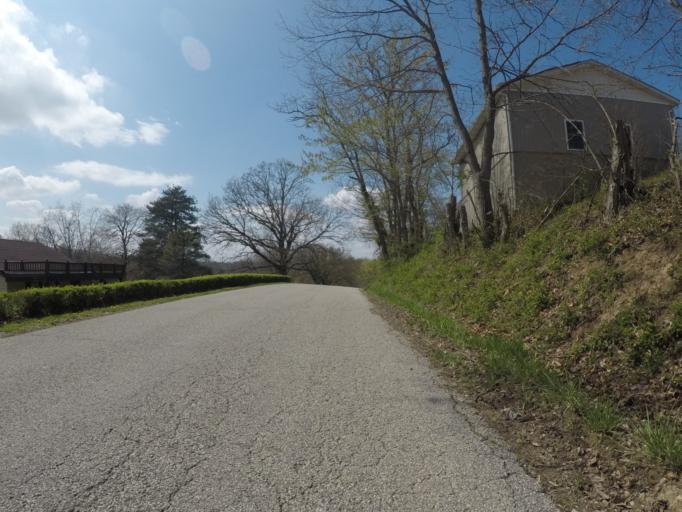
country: US
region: Ohio
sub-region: Lawrence County
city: Burlington
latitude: 38.3859
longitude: -82.5353
